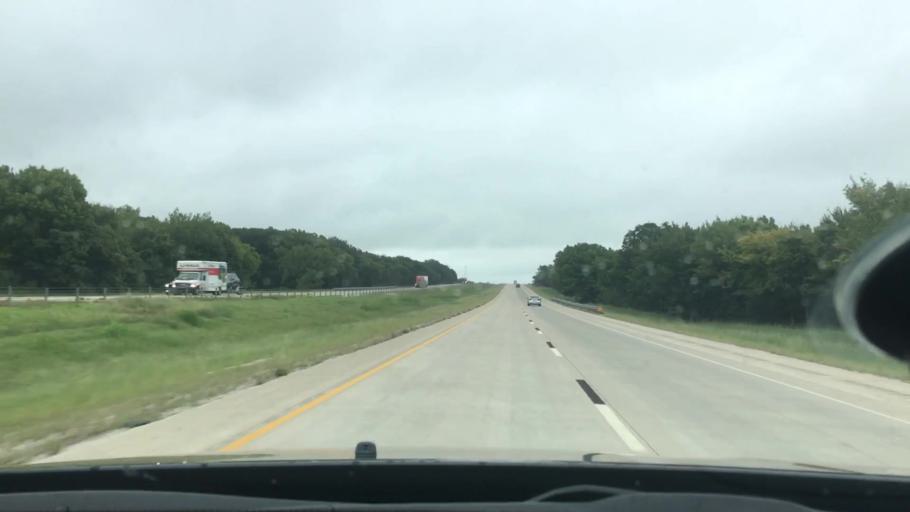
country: US
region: Oklahoma
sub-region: Okmulgee County
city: Wilson
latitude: 35.4275
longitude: -96.0825
